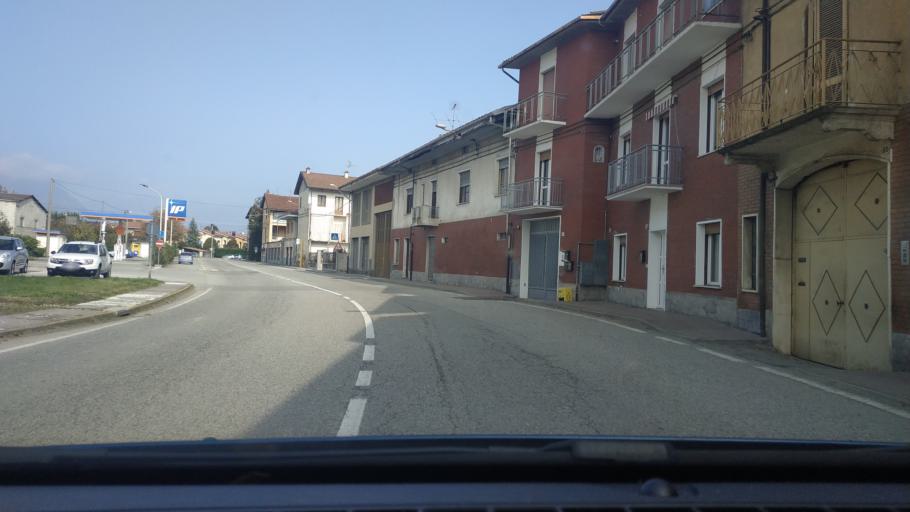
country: IT
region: Piedmont
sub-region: Provincia di Torino
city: Romano Canavese
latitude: 45.4004
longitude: 7.8688
